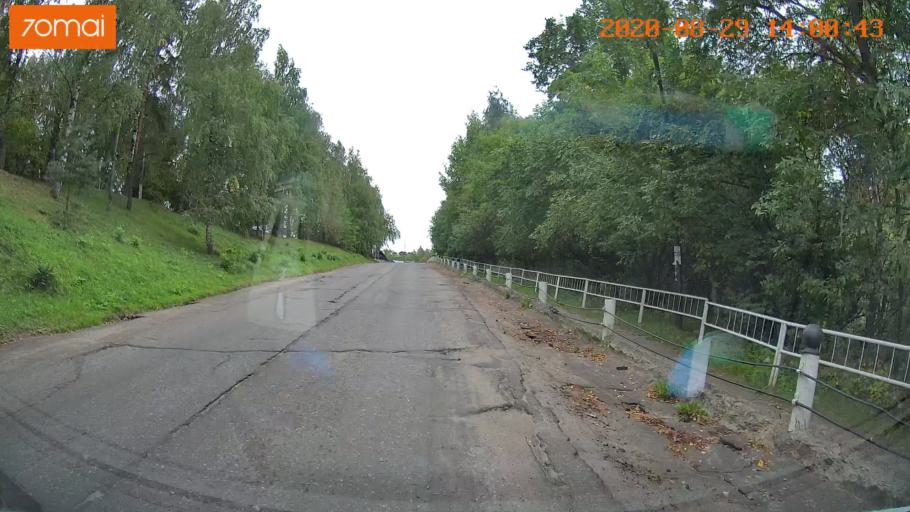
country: RU
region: Ivanovo
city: Yur'yevets
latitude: 57.3141
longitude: 43.1076
